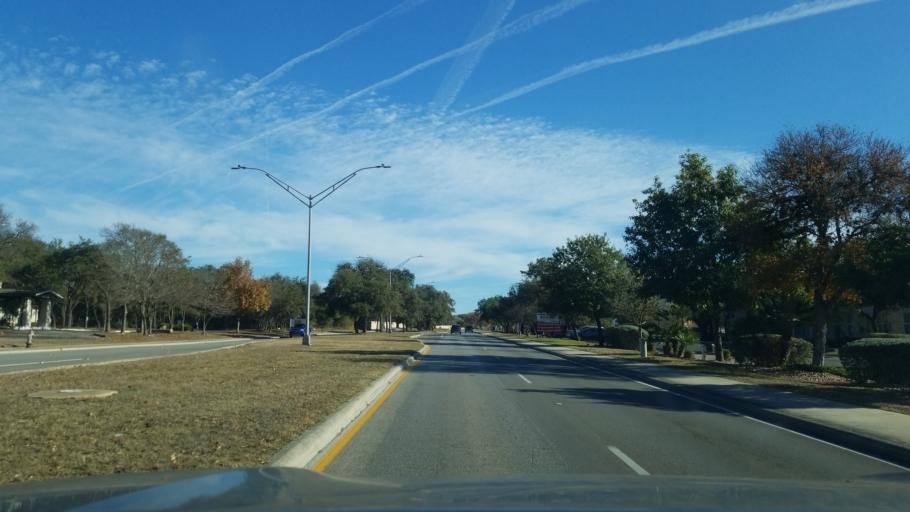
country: US
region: Texas
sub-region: Bexar County
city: Shavano Park
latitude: 29.5828
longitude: -98.5372
